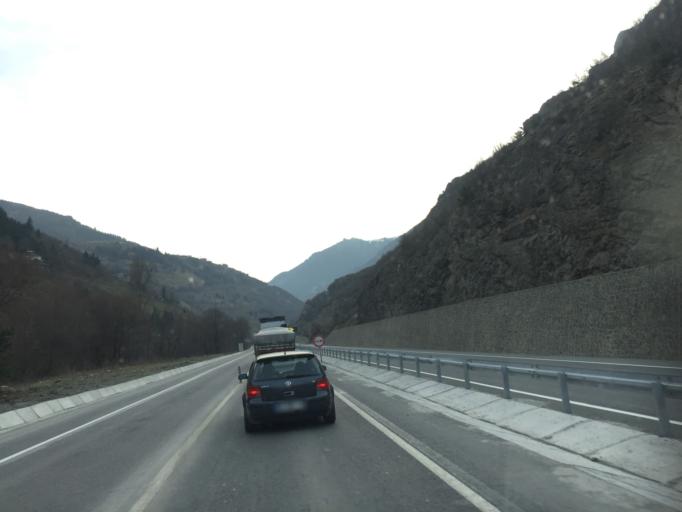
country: TR
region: Trabzon
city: Macka
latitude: 40.7949
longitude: 39.5833
